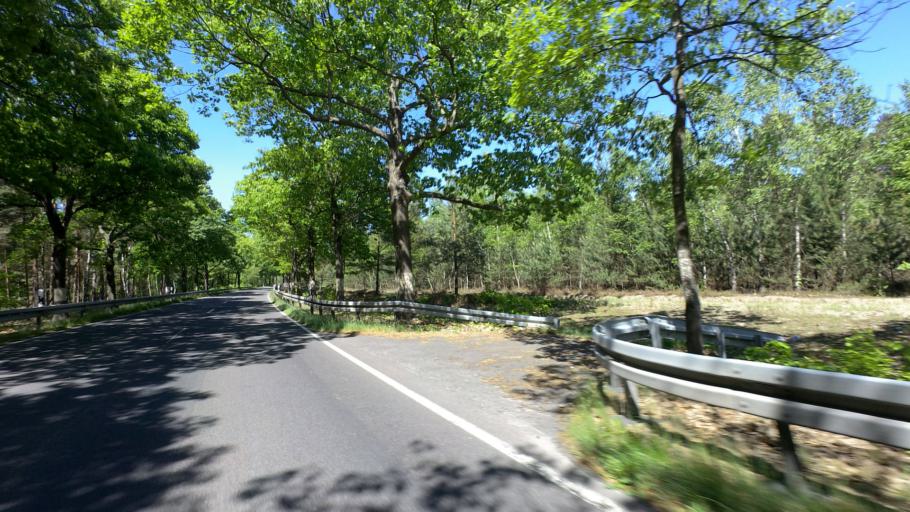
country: DE
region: Brandenburg
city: Drehnow
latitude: 51.9004
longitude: 14.3572
